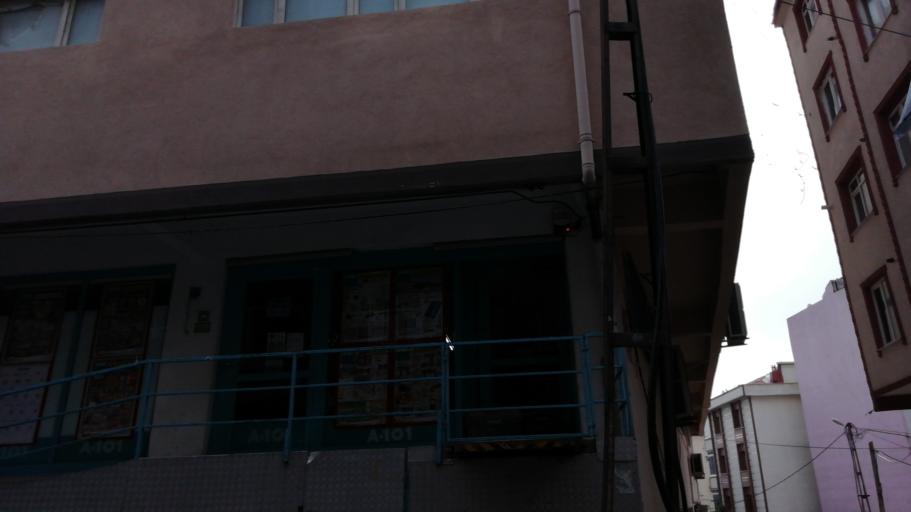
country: TR
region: Istanbul
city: Bagcilar
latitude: 41.0300
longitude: 28.8394
